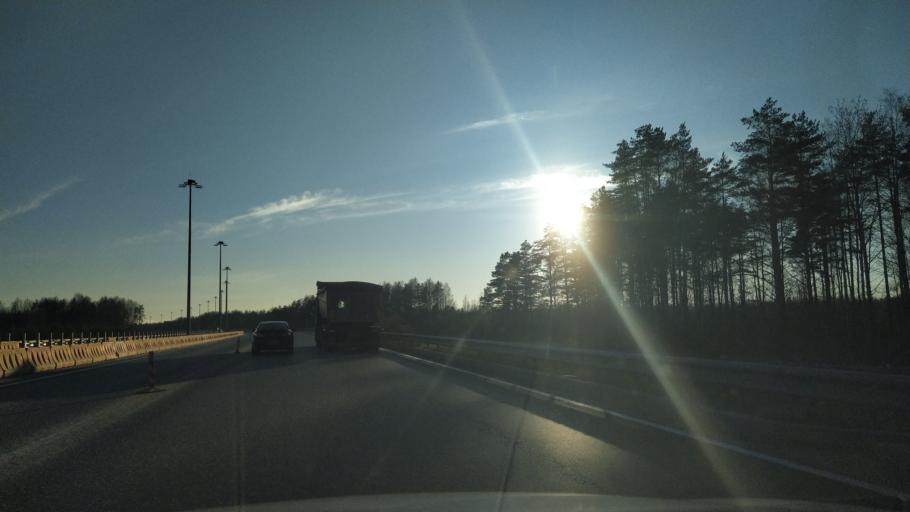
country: RU
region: St.-Petersburg
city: Levashovo
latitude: 60.0838
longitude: 30.2106
